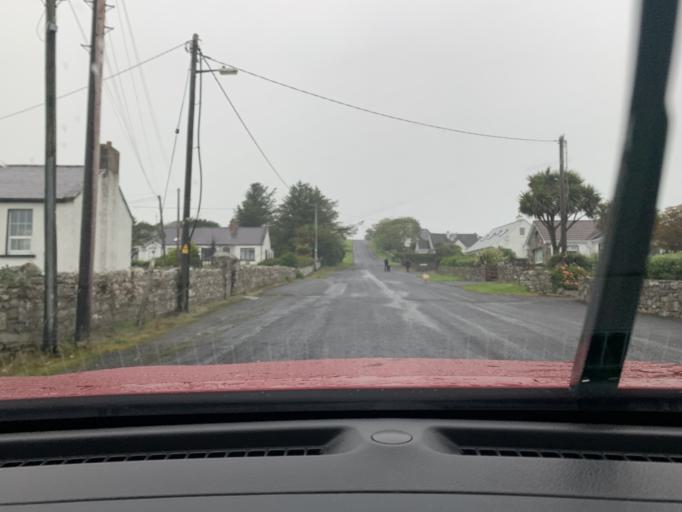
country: IE
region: Ulster
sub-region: County Donegal
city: Killybegs
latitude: 54.4668
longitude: -8.4500
